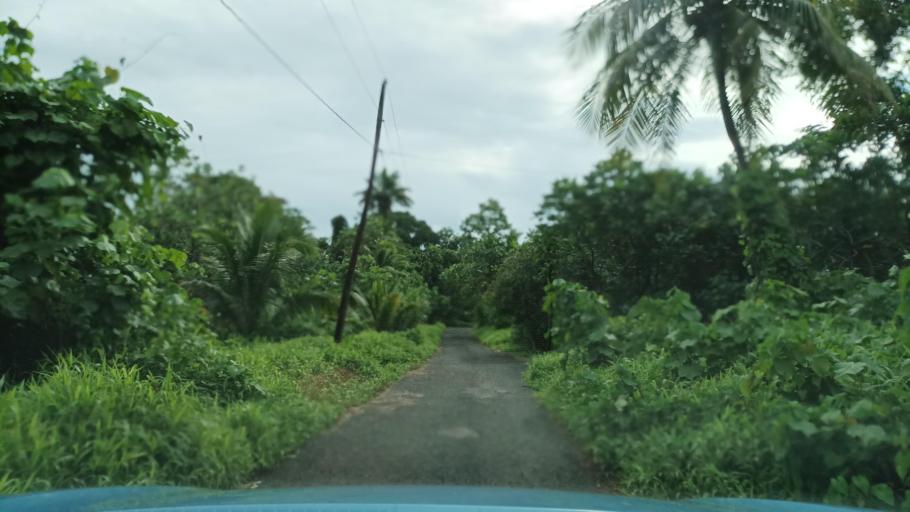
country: FM
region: Pohnpei
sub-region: Sokehs Municipality
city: Palikir - National Government Center
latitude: 6.8775
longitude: 158.1637
